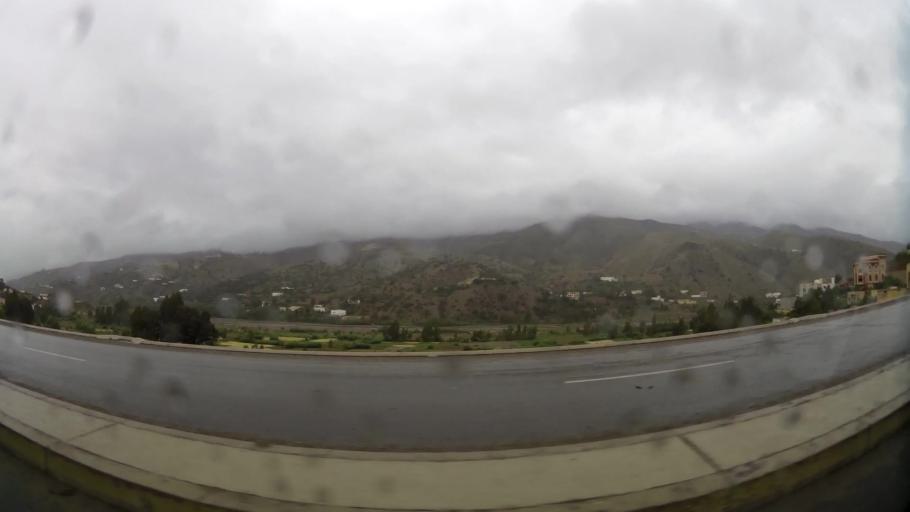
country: MA
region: Taza-Al Hoceima-Taounate
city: Imzourene
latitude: 35.0237
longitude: -3.8224
